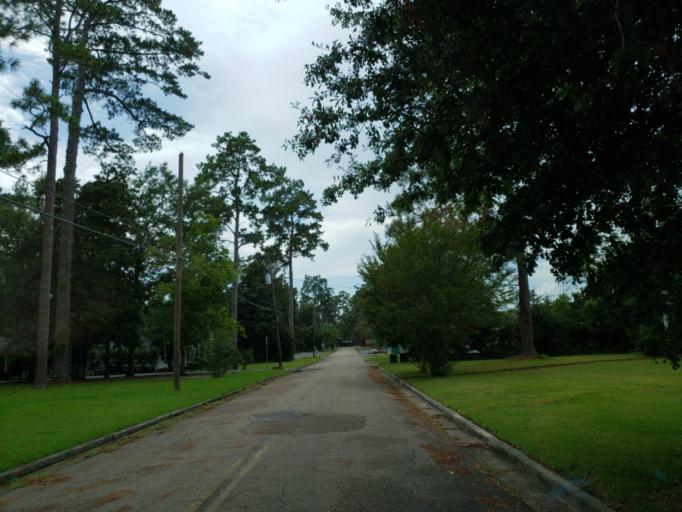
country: US
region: Mississippi
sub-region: Forrest County
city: Hattiesburg
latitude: 31.3229
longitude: -89.3120
